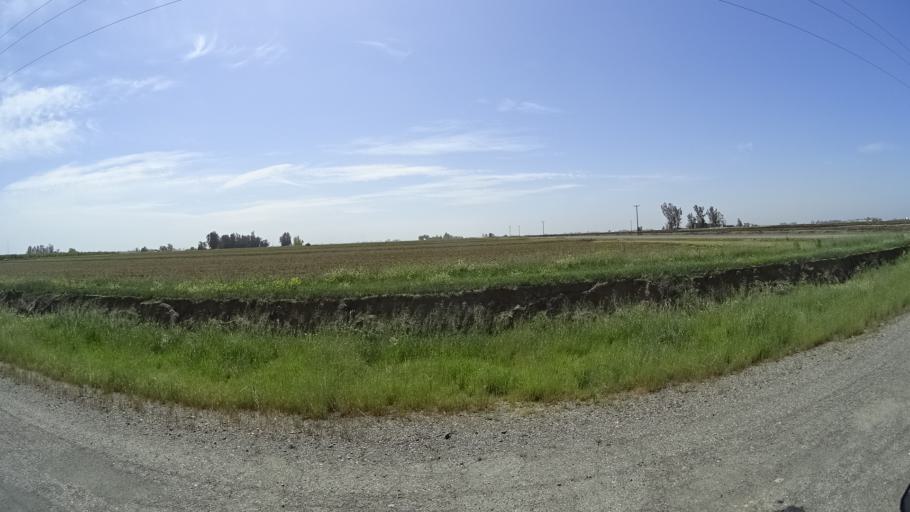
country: US
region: California
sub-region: Glenn County
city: Hamilton City
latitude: 39.6018
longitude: -122.0642
